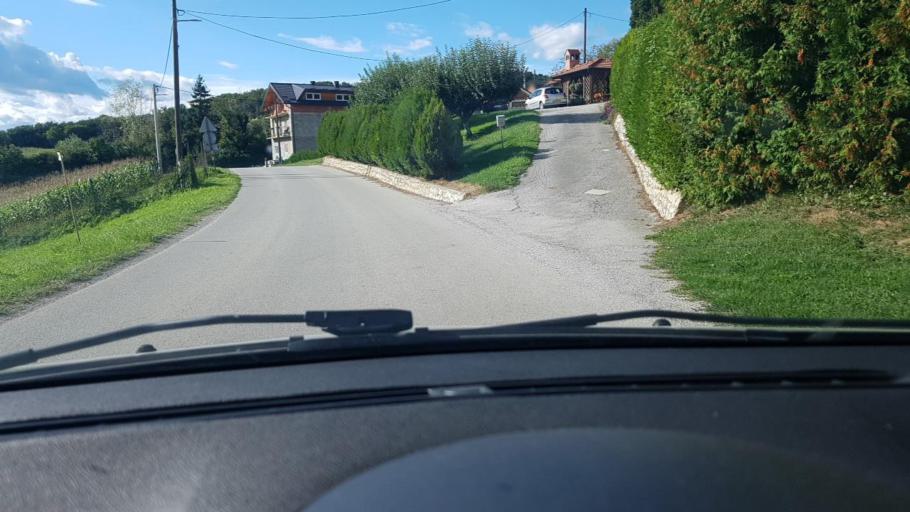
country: HR
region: Krapinsko-Zagorska
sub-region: Grad Krapina
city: Krapina
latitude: 46.1521
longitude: 15.8477
